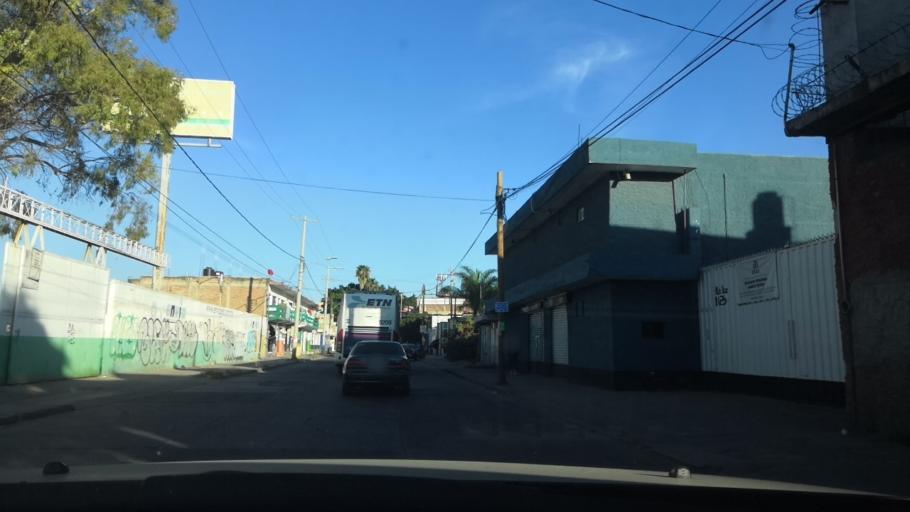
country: MX
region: Guanajuato
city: Leon
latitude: 21.1215
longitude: -101.6583
